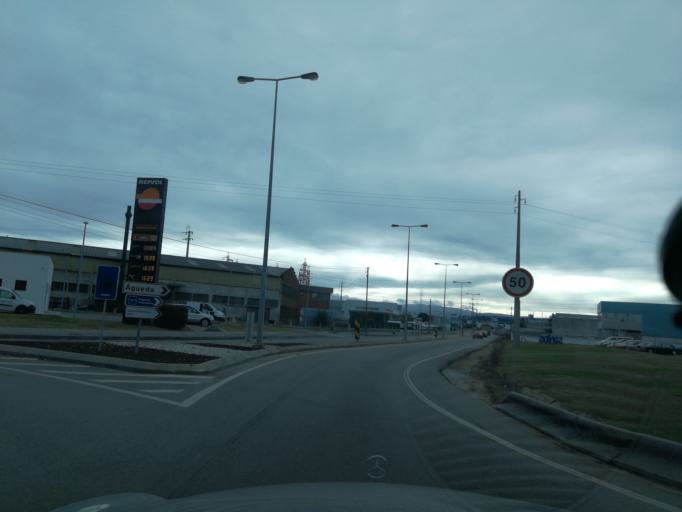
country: PT
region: Aveiro
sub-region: Agueda
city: Valongo
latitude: 40.5950
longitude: -8.4658
